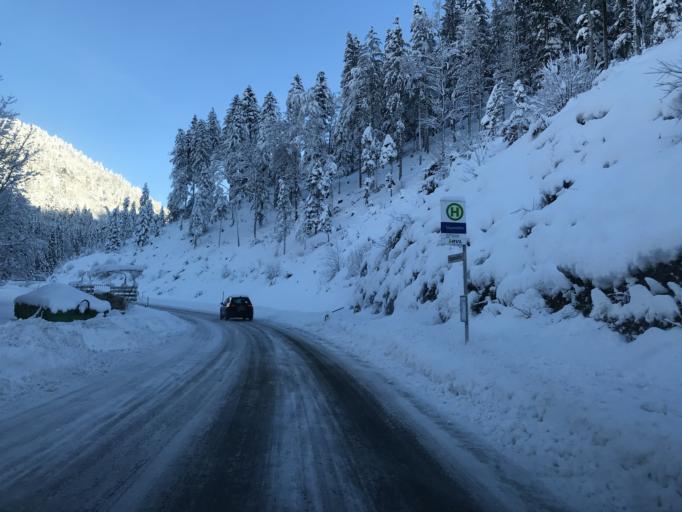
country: DE
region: Baden-Wuerttemberg
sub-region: Freiburg Region
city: Bollen
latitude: 47.7827
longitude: 7.8252
